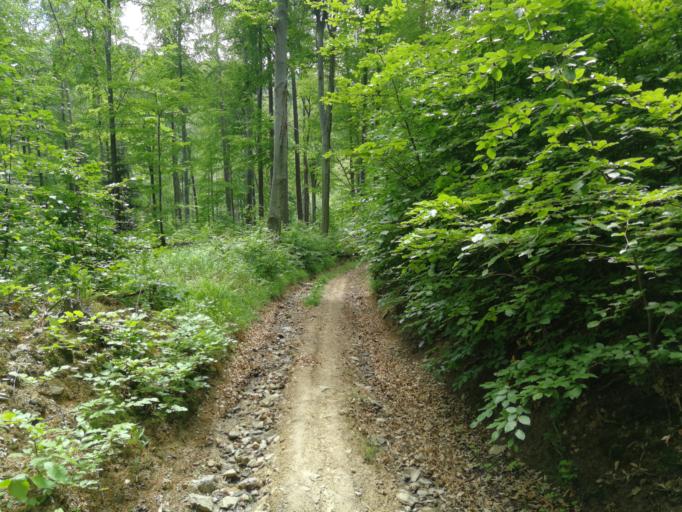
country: PL
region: Lesser Poland Voivodeship
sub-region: Powiat myslenicki
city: Osieczany
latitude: 49.8067
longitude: 19.9673
